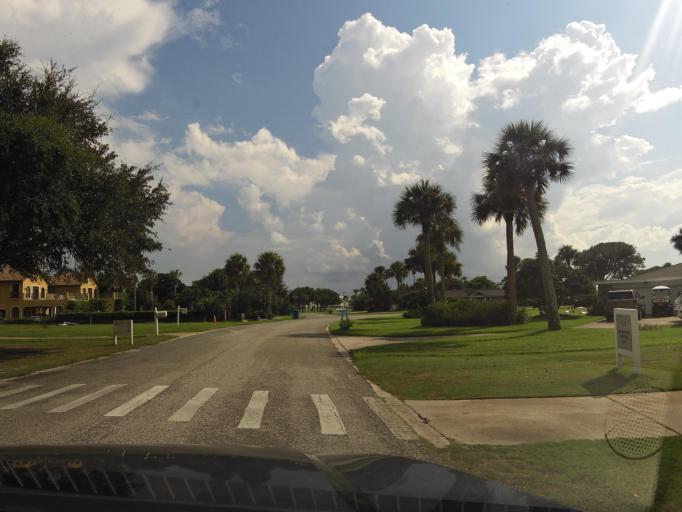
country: US
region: Florida
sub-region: Saint Johns County
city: Ponte Vedra Beach
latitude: 30.2494
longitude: -81.3826
